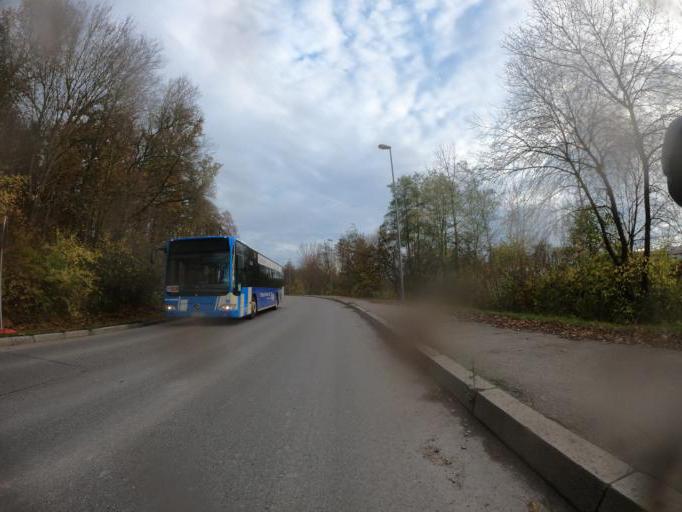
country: DE
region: Baden-Wuerttemberg
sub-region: Regierungsbezirk Stuttgart
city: Sindelfingen
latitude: 48.6973
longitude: 9.0237
